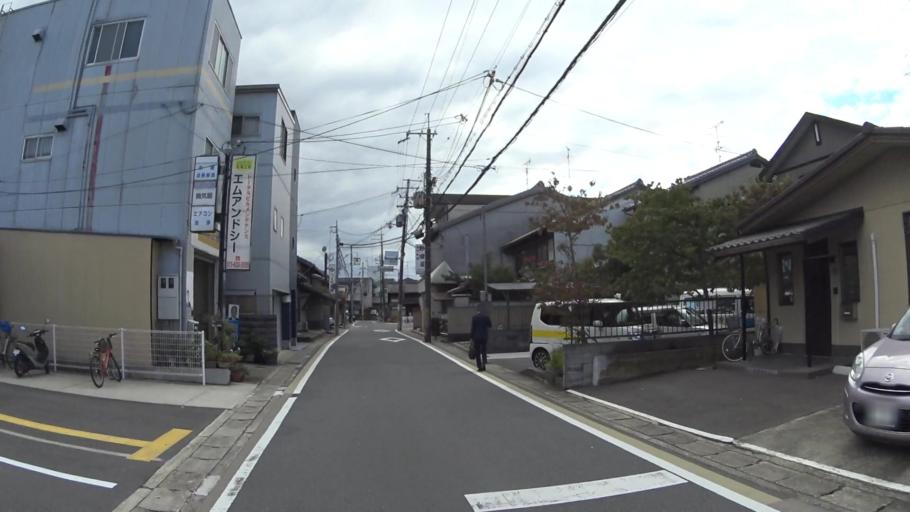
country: JP
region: Kyoto
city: Yawata
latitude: 34.9029
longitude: 135.7202
